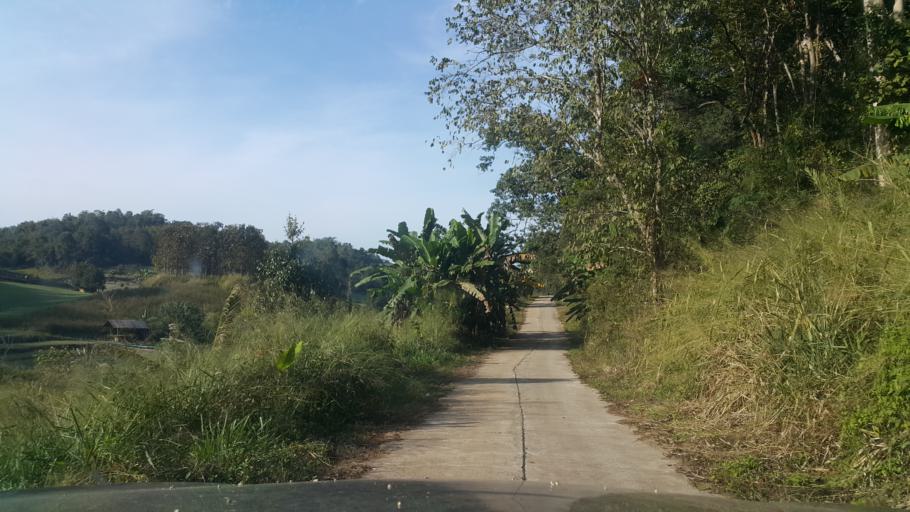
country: TH
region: Chiang Mai
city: Samoeng
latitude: 18.9869
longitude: 98.6850
